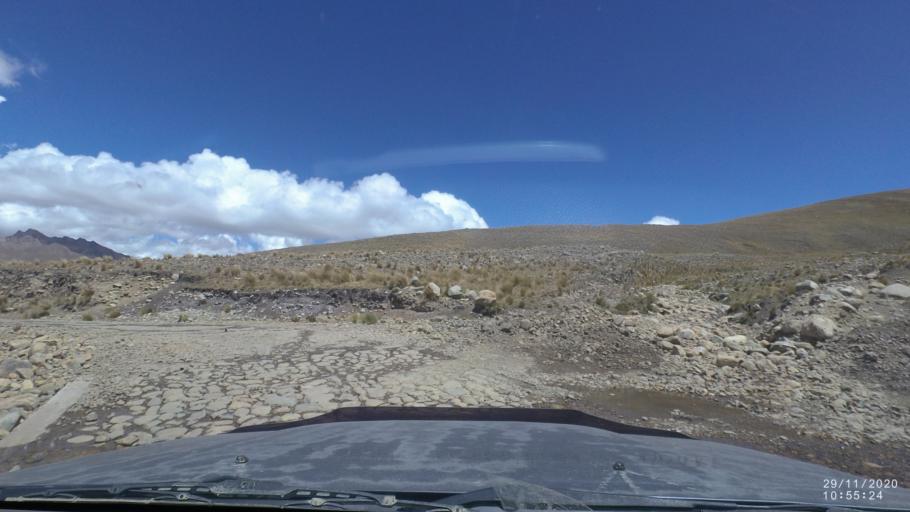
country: BO
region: Cochabamba
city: Cochabamba
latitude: -17.2228
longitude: -66.2211
